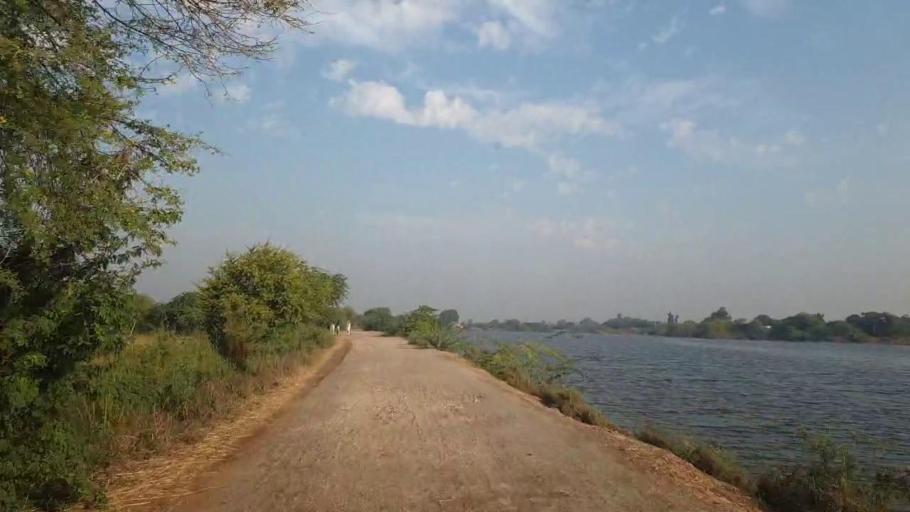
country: PK
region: Sindh
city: Tando Bago
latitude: 24.8004
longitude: 68.9599
